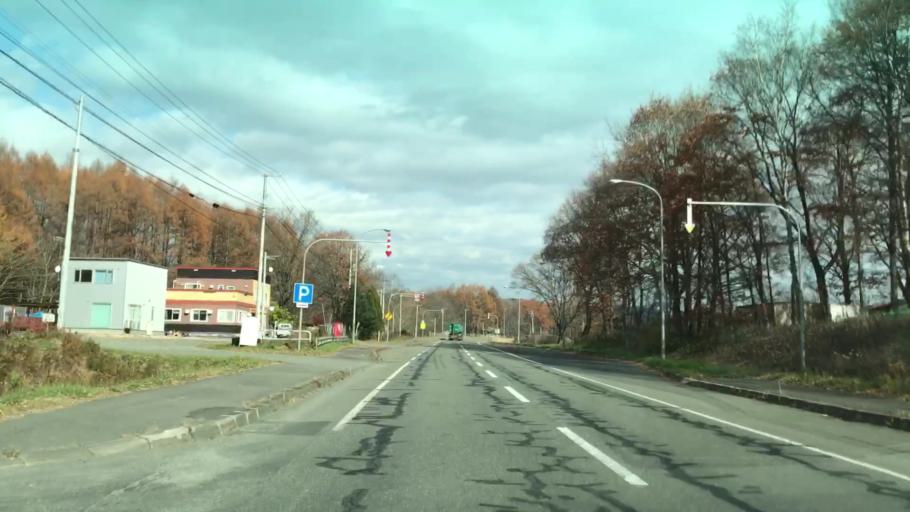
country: JP
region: Hokkaido
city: Shizunai-furukawacho
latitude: 42.6936
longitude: 142.2164
